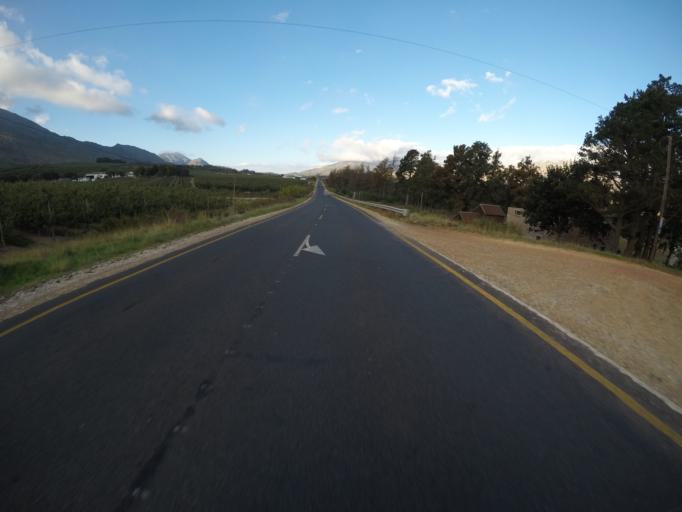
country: ZA
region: Western Cape
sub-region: Overberg District Municipality
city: Caledon
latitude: -34.0129
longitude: 19.2624
